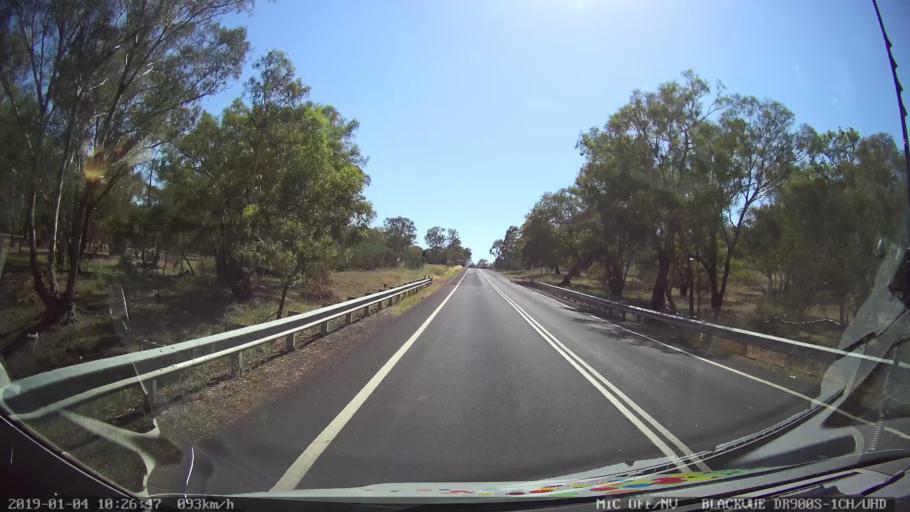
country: AU
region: New South Wales
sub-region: Cabonne
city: Canowindra
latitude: -33.3750
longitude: 148.5905
